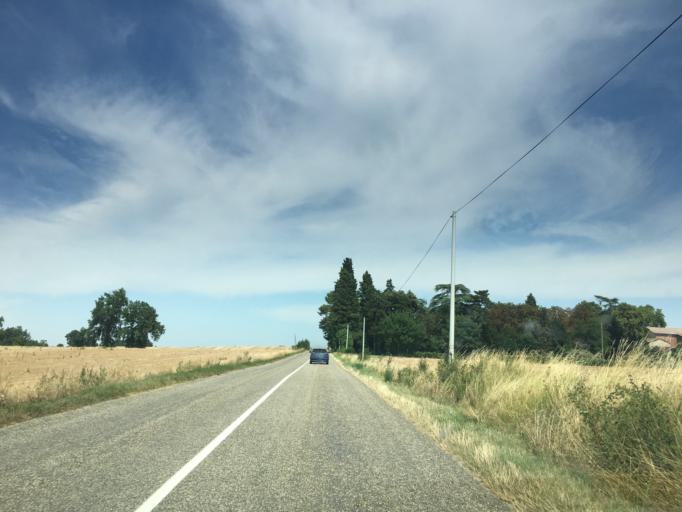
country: FR
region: Midi-Pyrenees
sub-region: Departement du Gers
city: Fleurance
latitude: 43.8724
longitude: 0.7525
